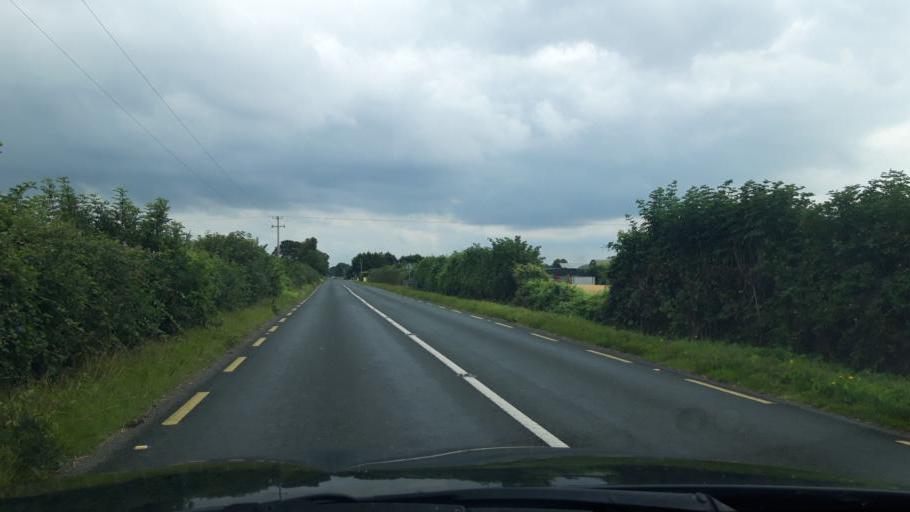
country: IE
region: Leinster
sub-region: Kildare
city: Athy
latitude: 53.0216
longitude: -7.0057
